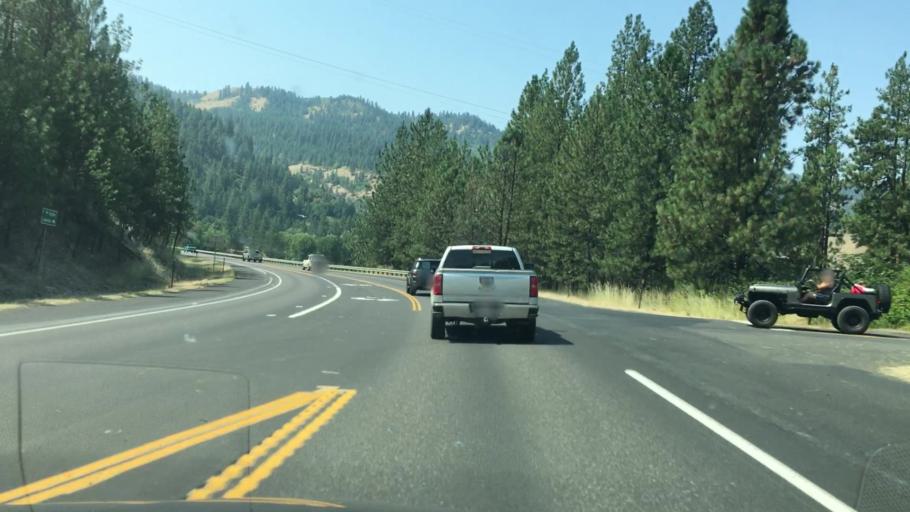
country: US
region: Idaho
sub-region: Nez Perce County
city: Lapwai
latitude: 46.5099
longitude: -116.5617
